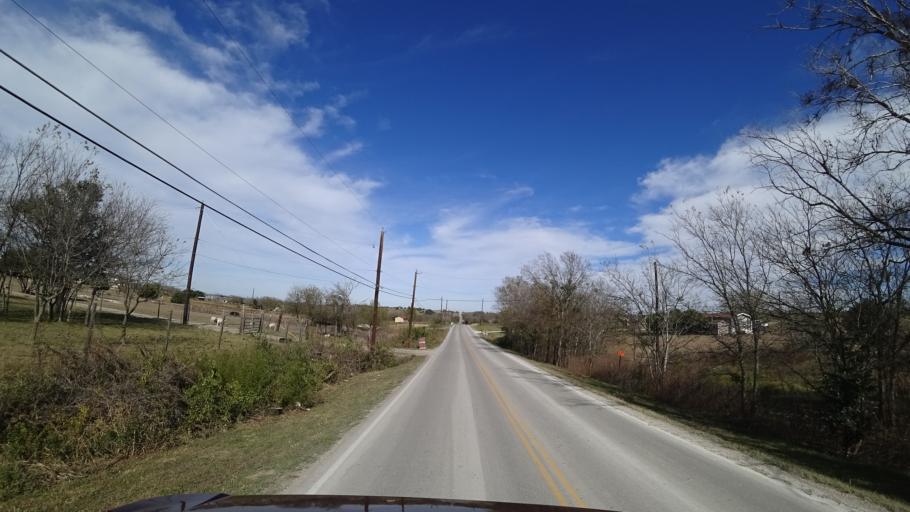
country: US
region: Texas
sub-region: Travis County
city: Onion Creek
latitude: 30.1220
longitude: -97.7423
